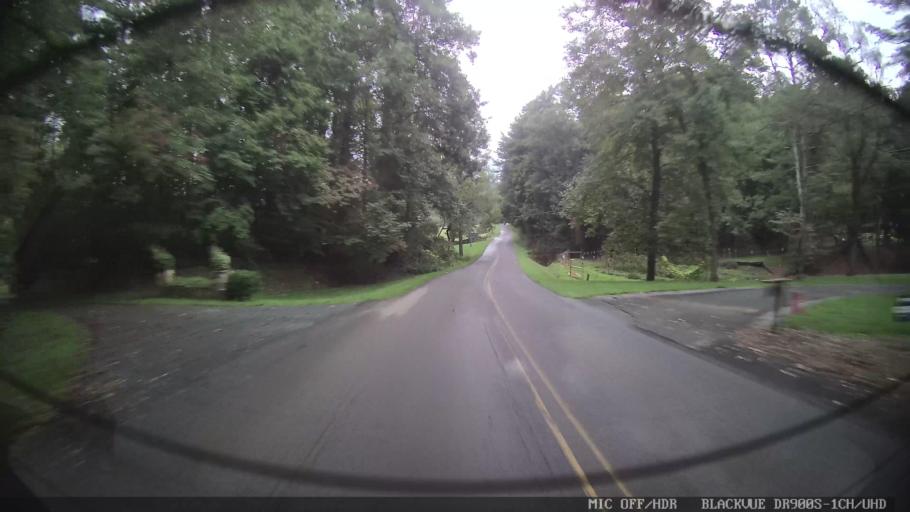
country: US
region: Georgia
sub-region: Gilmer County
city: Ellijay
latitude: 34.7598
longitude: -84.5315
